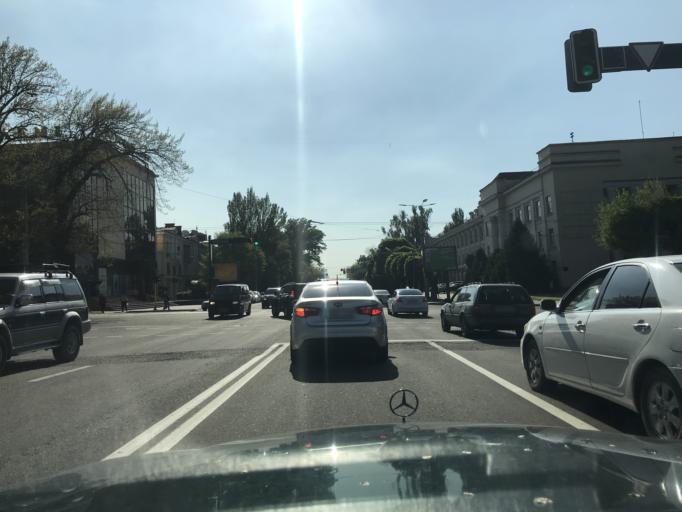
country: KZ
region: Almaty Qalasy
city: Almaty
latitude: 43.2547
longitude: 76.9420
